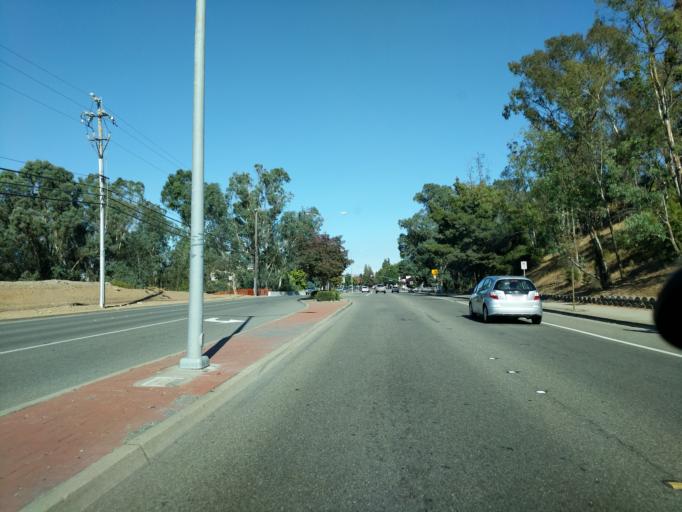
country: US
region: California
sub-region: Alameda County
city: Livermore
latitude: 37.6777
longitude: -121.7903
